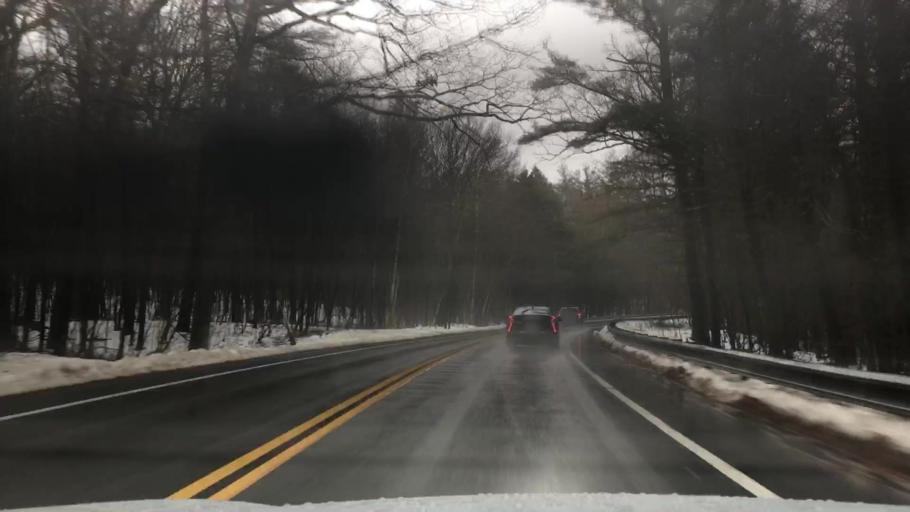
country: US
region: Massachusetts
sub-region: Franklin County
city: Shutesbury
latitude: 42.4331
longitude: -72.3953
